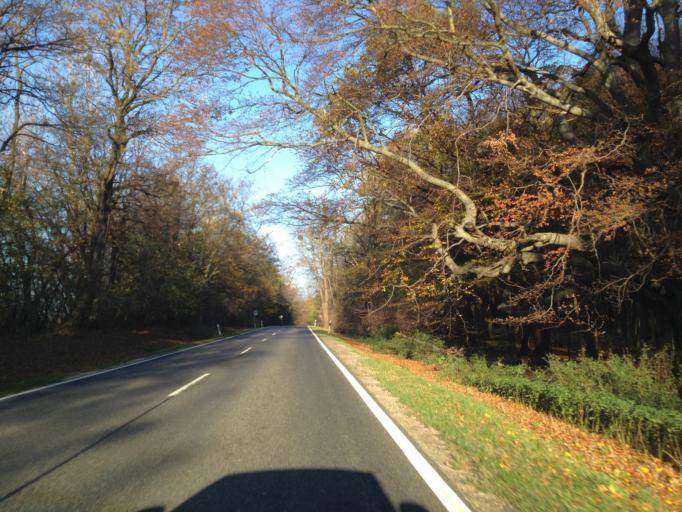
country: HU
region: Veszprem
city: Zirc
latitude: 47.3319
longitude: 17.8823
